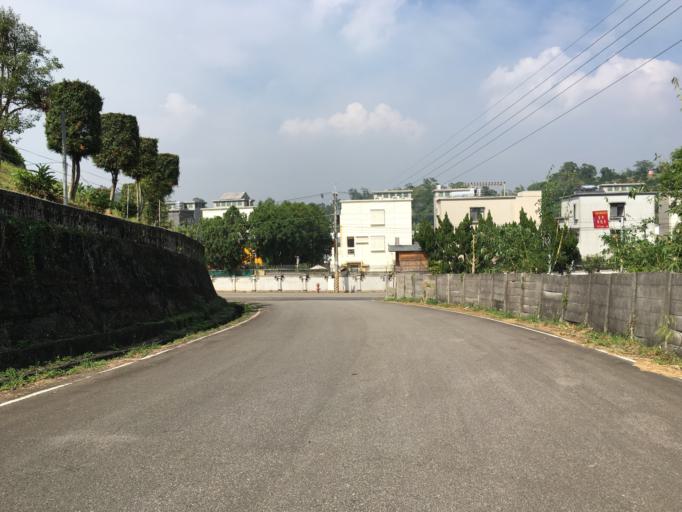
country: TW
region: Taiwan
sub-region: Taichung City
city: Taichung
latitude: 24.1793
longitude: 120.7571
